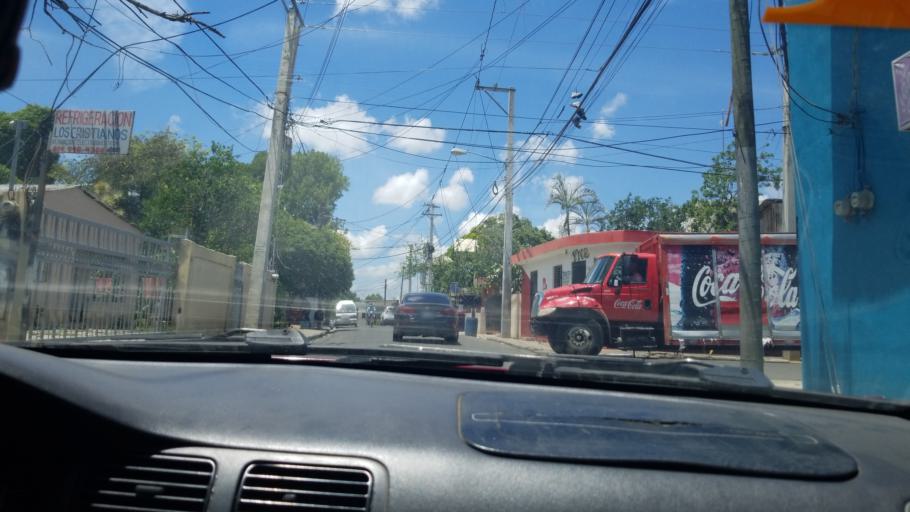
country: DO
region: Santiago
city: Santiago de los Caballeros
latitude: 19.4827
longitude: -70.6874
